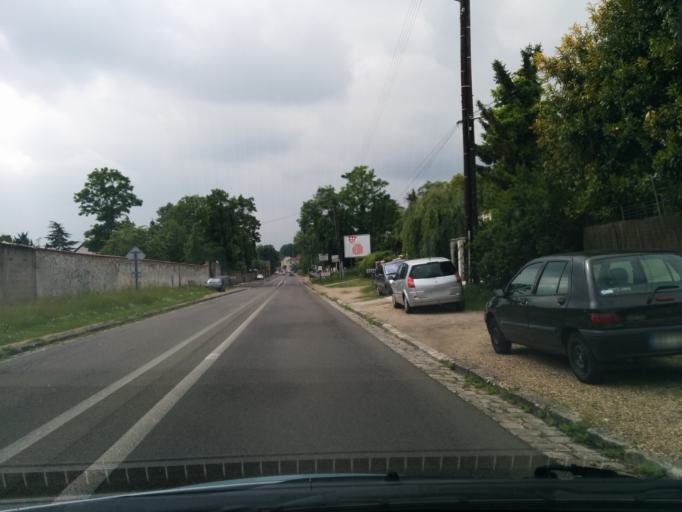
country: FR
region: Ile-de-France
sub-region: Departement des Yvelines
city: Meulan-en-Yvelines
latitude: 49.0091
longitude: 1.9377
